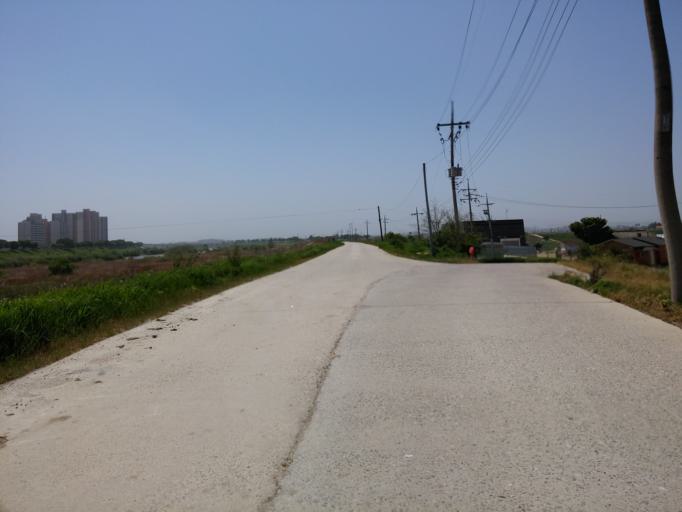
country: KR
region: Chungcheongnam-do
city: Nonsan
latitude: 36.2161
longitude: 127.0980
